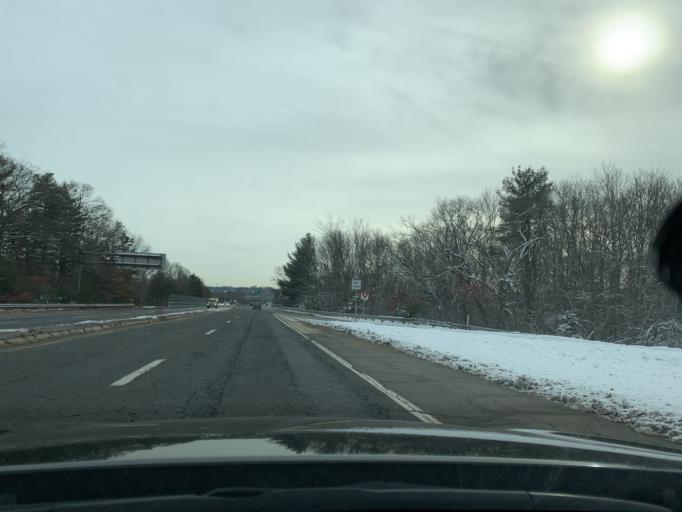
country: US
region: Massachusetts
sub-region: Norfolk County
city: Canton
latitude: 42.1721
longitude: -71.1728
